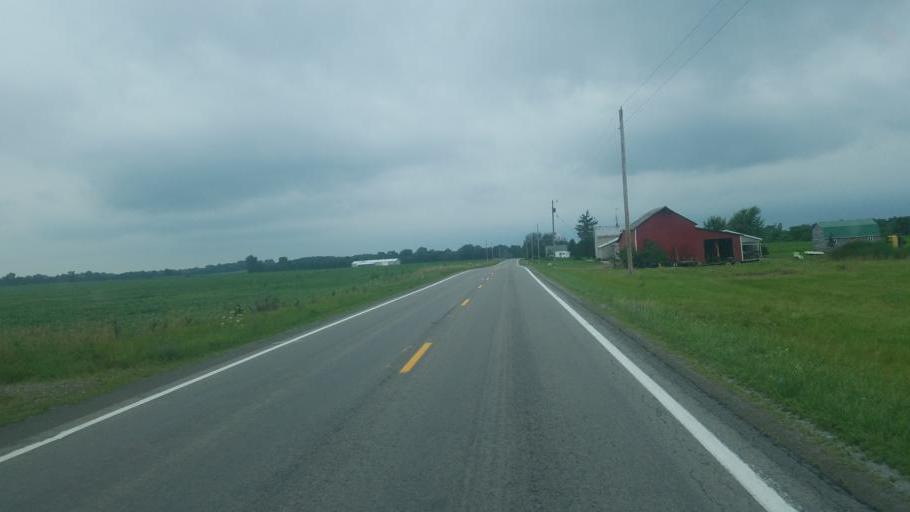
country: US
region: Ohio
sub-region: Logan County
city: Northwood
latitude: 40.5922
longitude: -83.7714
